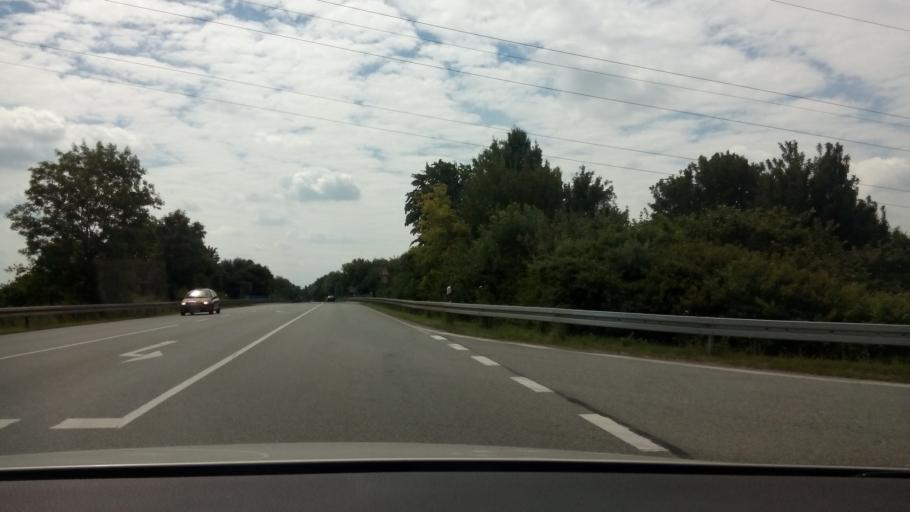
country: DE
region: Bavaria
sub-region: Upper Bavaria
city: Marzling
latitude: 48.3886
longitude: 11.7782
